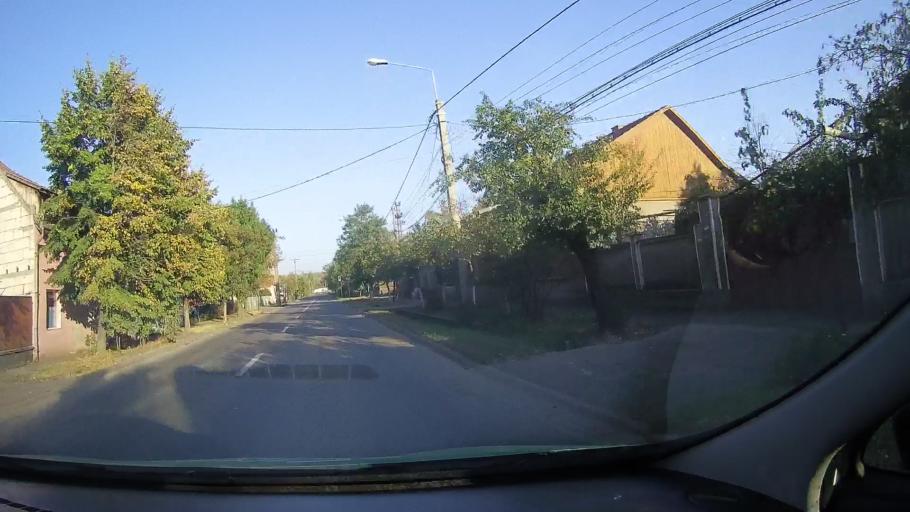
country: RO
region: Bihor
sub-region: Comuna Santandrei
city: Santandrei
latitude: 47.1035
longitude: 21.8887
